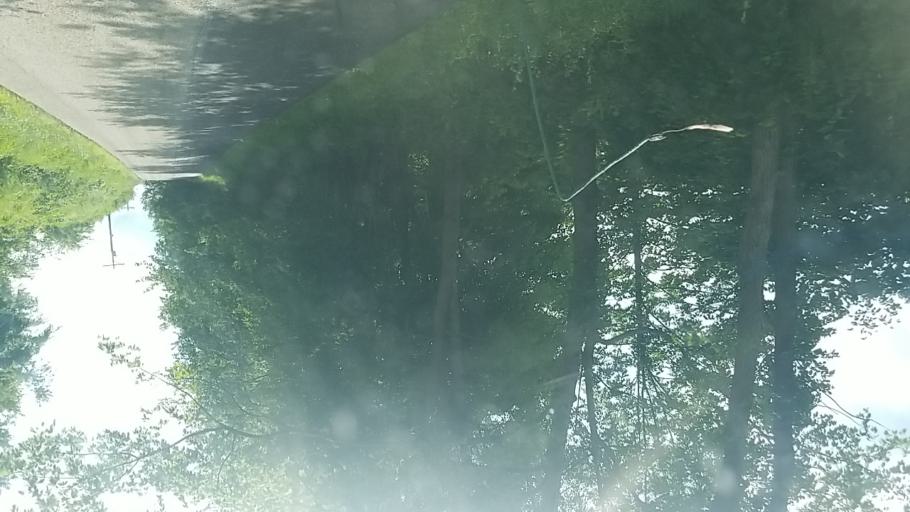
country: US
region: Ohio
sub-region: Richland County
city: Lincoln Heights
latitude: 40.6796
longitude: -82.3750
